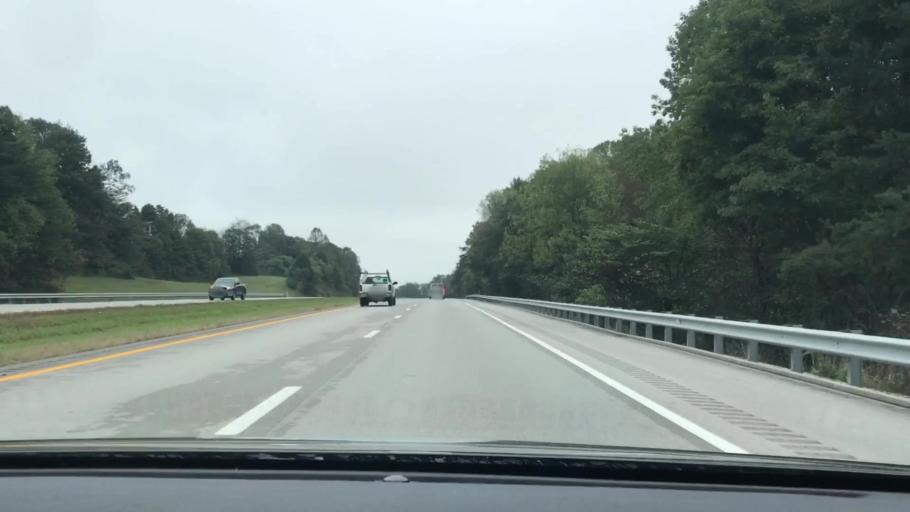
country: US
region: Kentucky
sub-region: Pulaski County
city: Somerset
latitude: 37.0944
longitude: -84.8228
